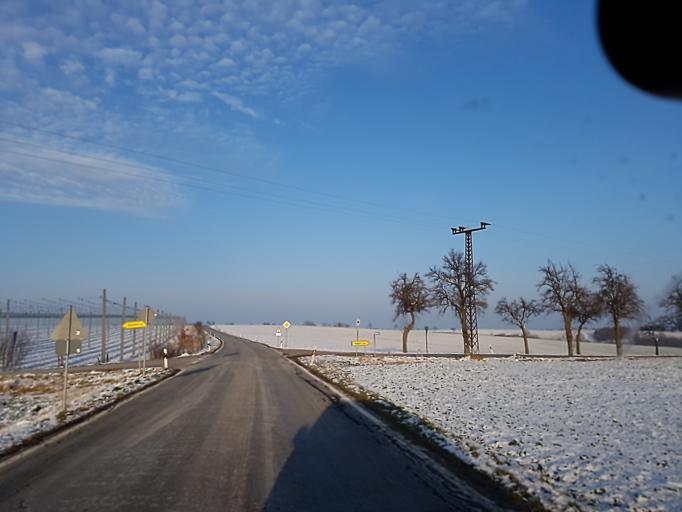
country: DE
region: Saxony
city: Grossweitzschen
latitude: 51.1979
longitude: 13.0730
